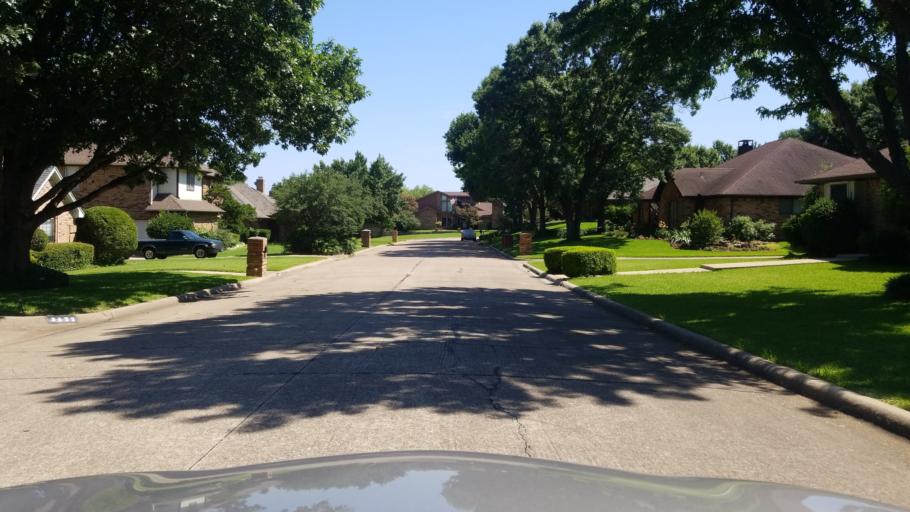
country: US
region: Texas
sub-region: Dallas County
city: Grand Prairie
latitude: 32.6853
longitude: -96.9969
